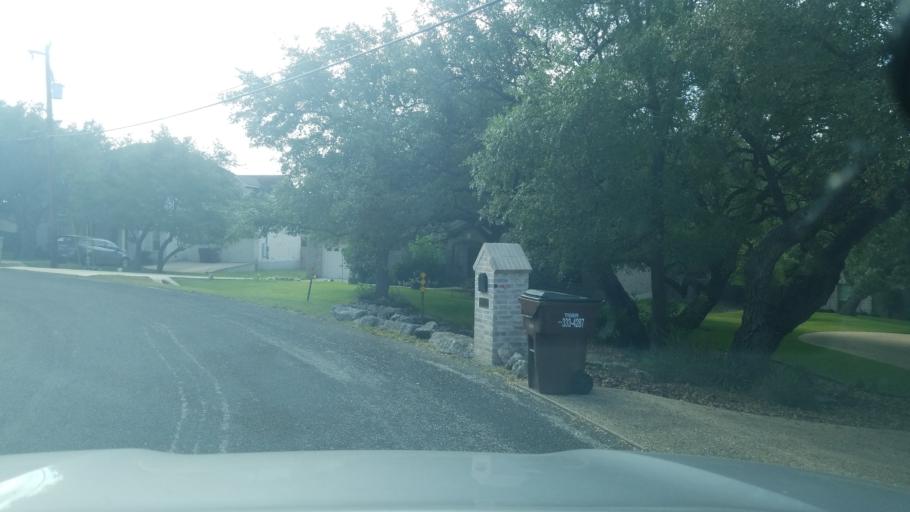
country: US
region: Texas
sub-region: Bexar County
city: Timberwood Park
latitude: 29.6937
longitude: -98.5004
